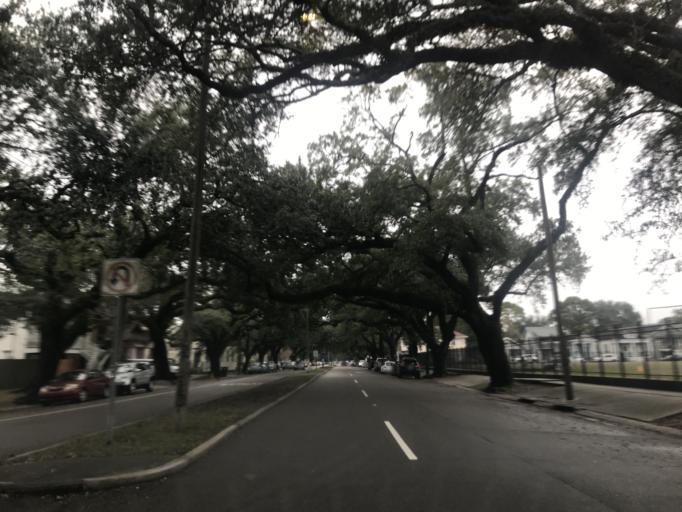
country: US
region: Louisiana
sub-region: Orleans Parish
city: New Orleans
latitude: 29.9730
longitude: -90.1046
